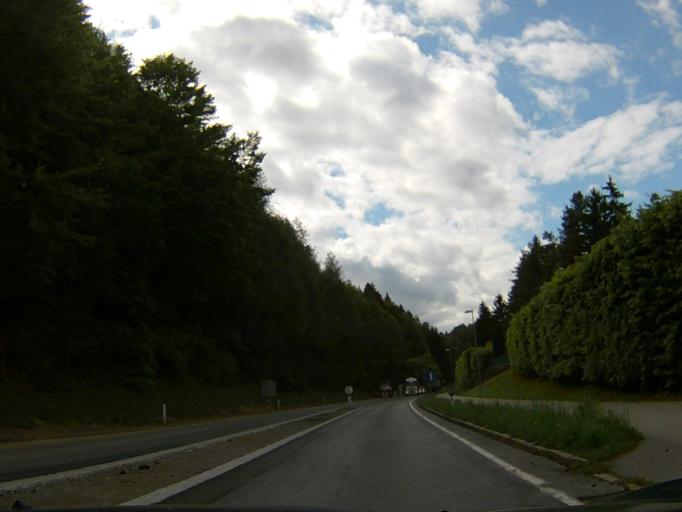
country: AT
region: Carinthia
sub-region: Politischer Bezirk Villach Land
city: Fresach
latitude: 46.6621
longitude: 13.7396
